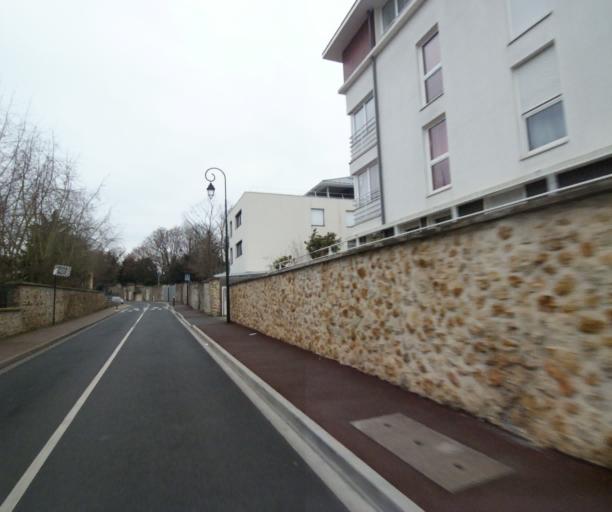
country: FR
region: Ile-de-France
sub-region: Departement des Hauts-de-Seine
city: Vaucresson
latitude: 48.8397
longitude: 2.1609
